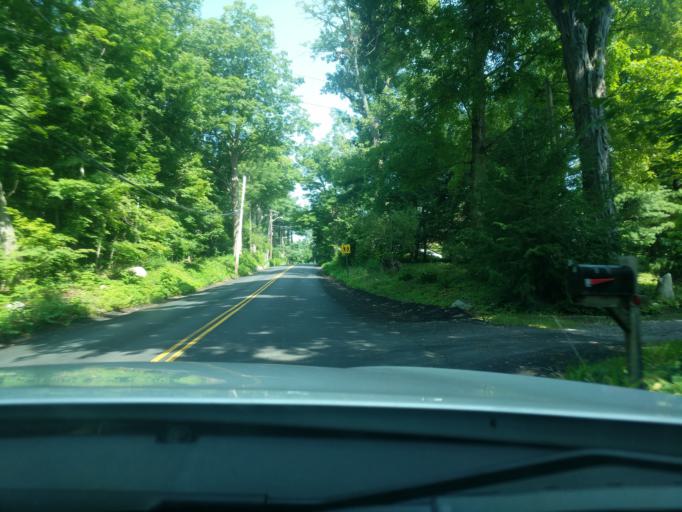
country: US
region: Massachusetts
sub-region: Berkshire County
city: Great Barrington
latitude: 42.2054
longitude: -73.3598
